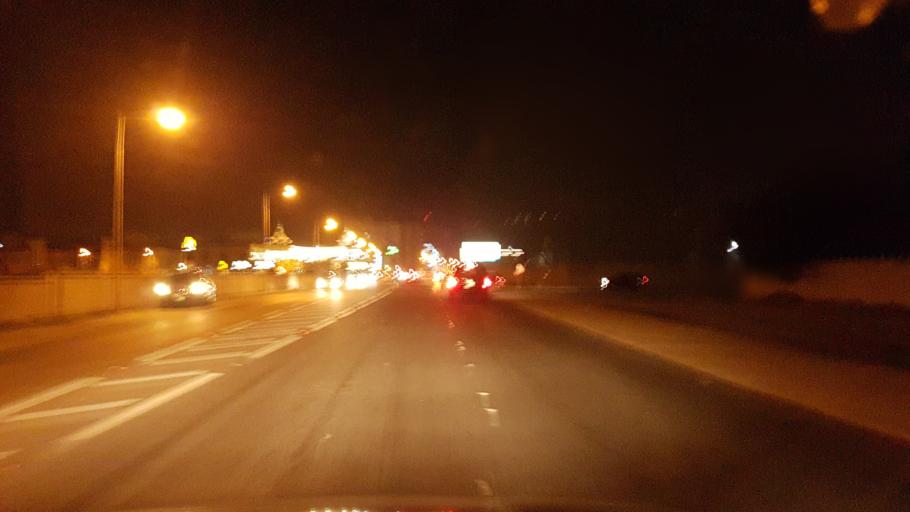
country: BH
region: Central Governorate
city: Madinat Hamad
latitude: 26.1766
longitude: 50.4810
